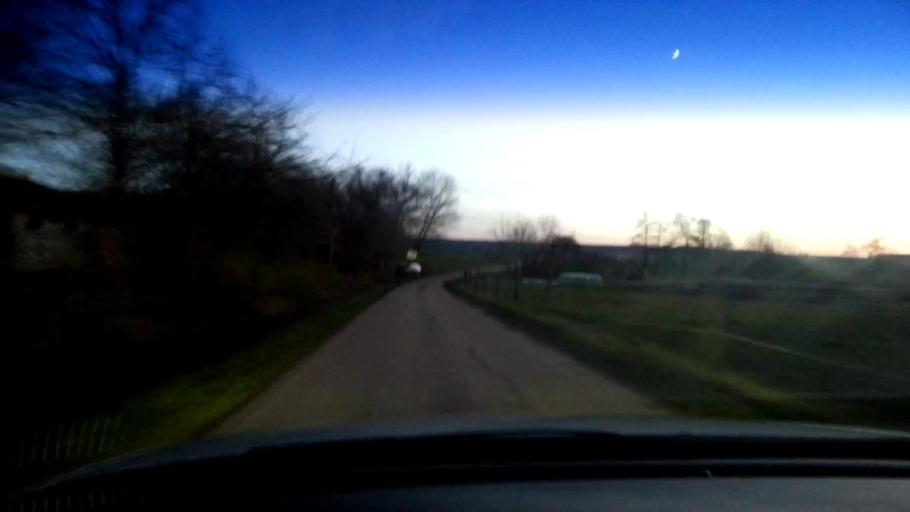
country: DE
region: Bavaria
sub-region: Upper Franconia
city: Schesslitz
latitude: 49.9546
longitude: 10.9970
